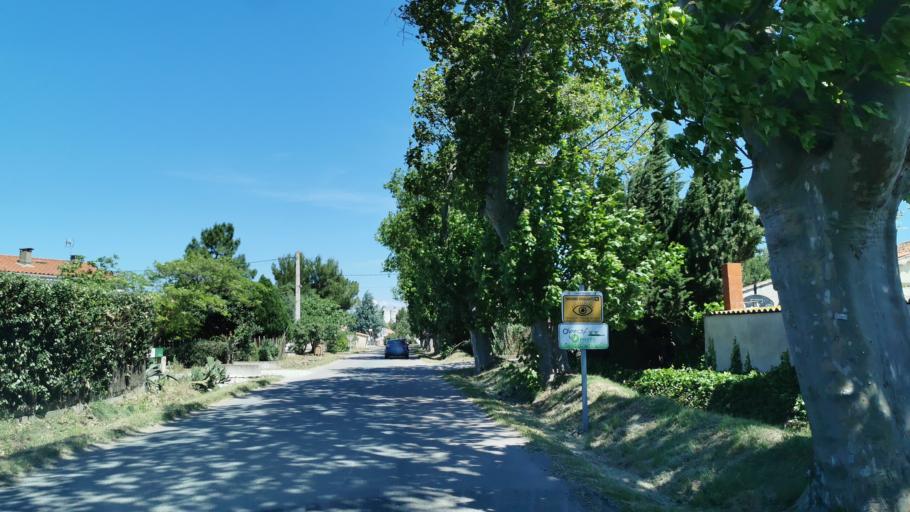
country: FR
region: Languedoc-Roussillon
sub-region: Departement de l'Aude
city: Canet
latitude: 43.2197
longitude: 2.8459
